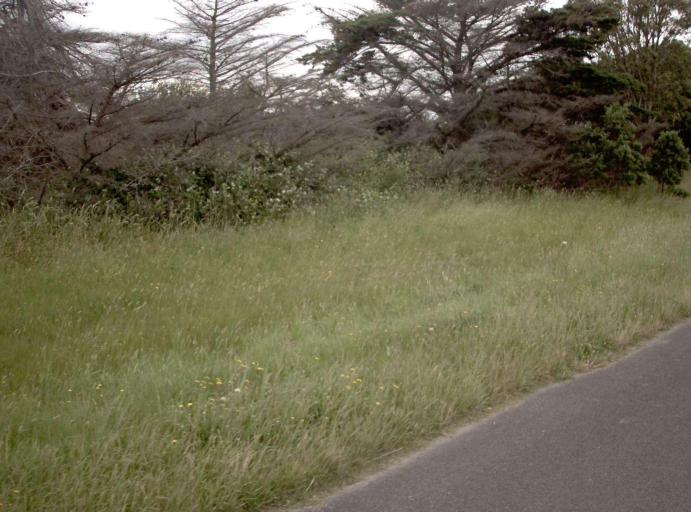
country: AU
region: Victoria
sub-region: Cardinia
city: Koo-Wee-Rup
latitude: -38.2277
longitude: 145.5099
